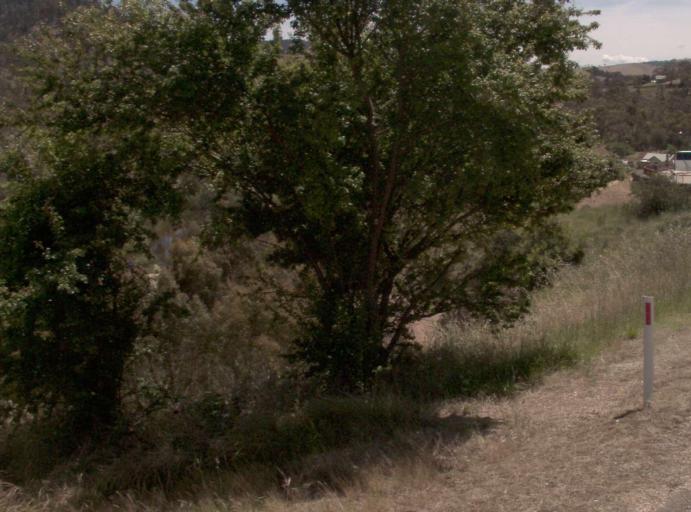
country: AU
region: Victoria
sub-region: Alpine
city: Mount Beauty
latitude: -37.1016
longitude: 147.5891
